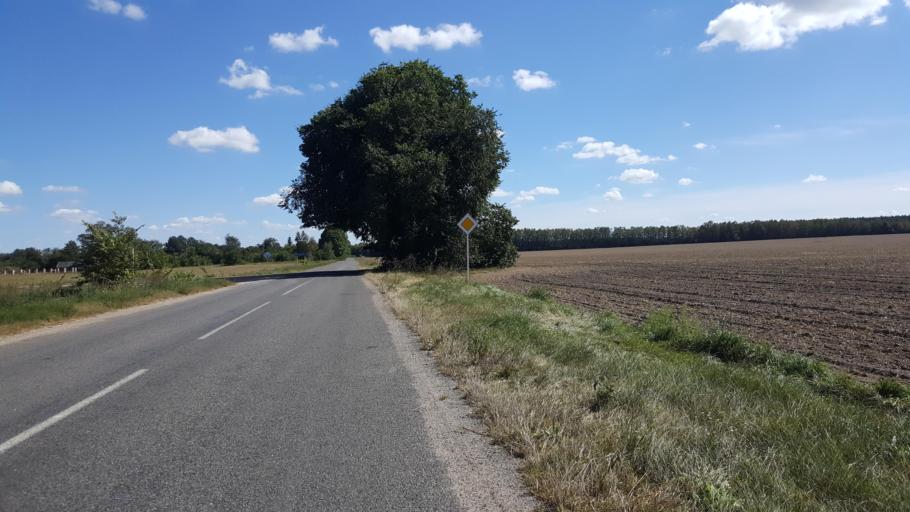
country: BY
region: Brest
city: Vysokaye
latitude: 52.2771
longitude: 23.3560
